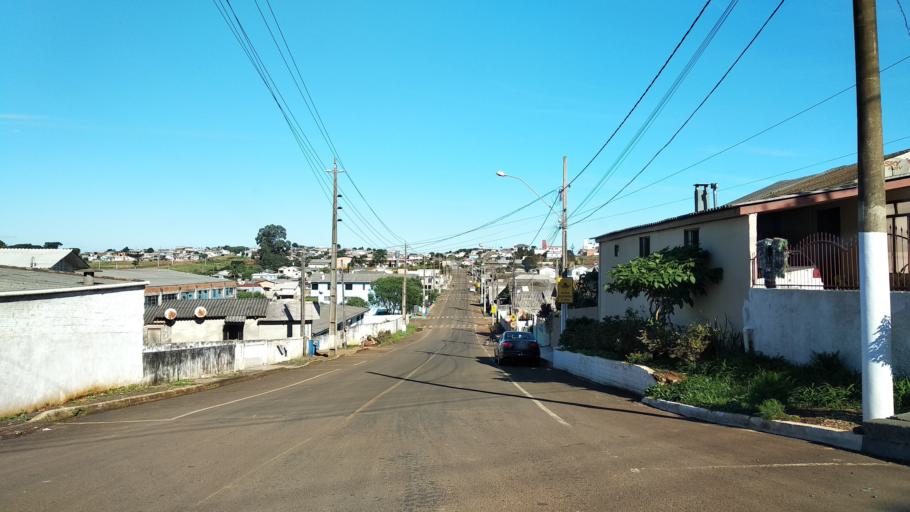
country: BR
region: Santa Catarina
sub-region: Campos Novos
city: Campos Novos
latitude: -27.3844
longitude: -51.2110
